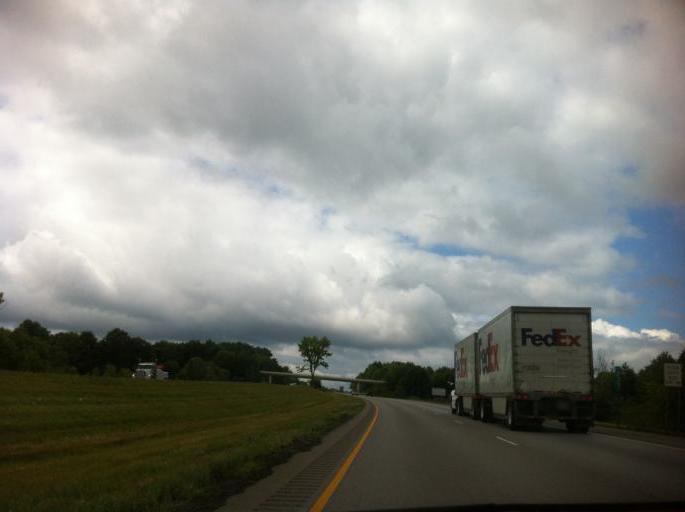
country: US
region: Ohio
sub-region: Trumbull County
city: Masury
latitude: 41.1835
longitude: -80.5233
